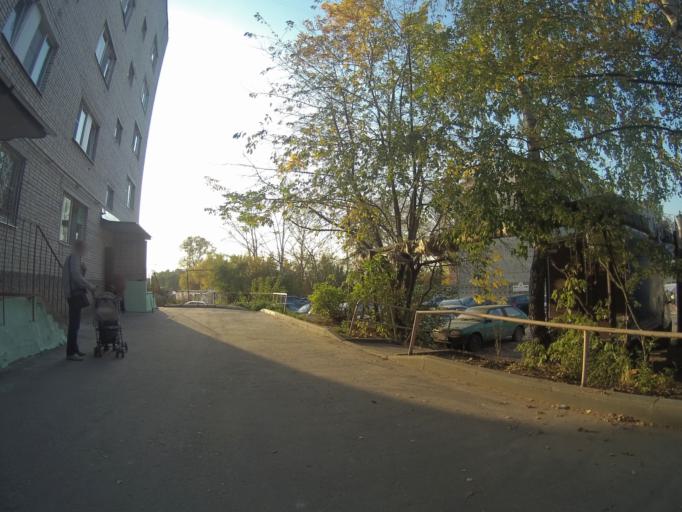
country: RU
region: Vladimir
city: Vladimir
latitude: 56.1204
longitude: 40.3456
